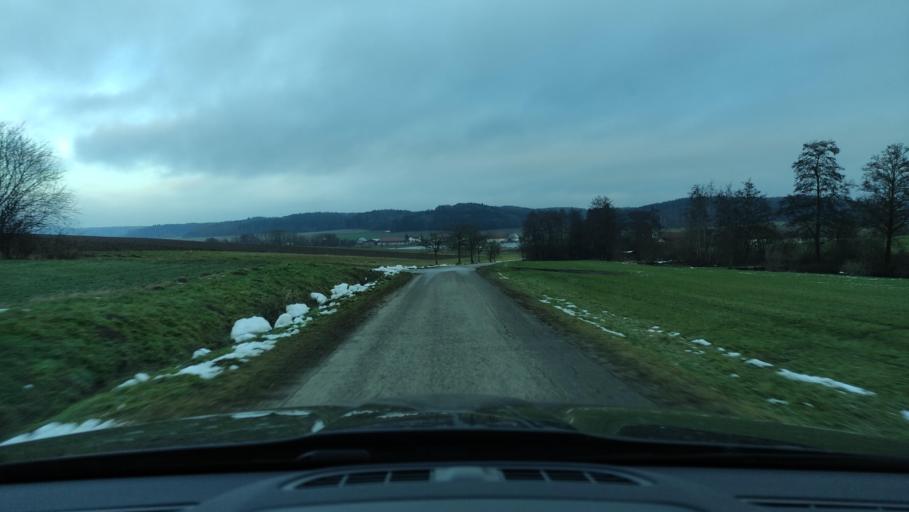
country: DE
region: Bavaria
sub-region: Swabia
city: Deisenhausen
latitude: 48.2834
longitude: 10.3496
